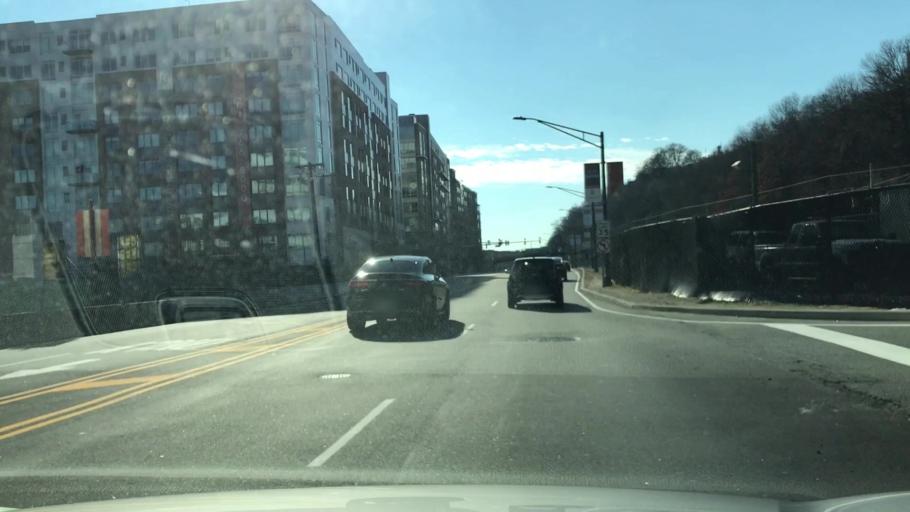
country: US
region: New Jersey
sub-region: Hudson County
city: Weehawken
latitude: 40.7752
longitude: -74.0126
